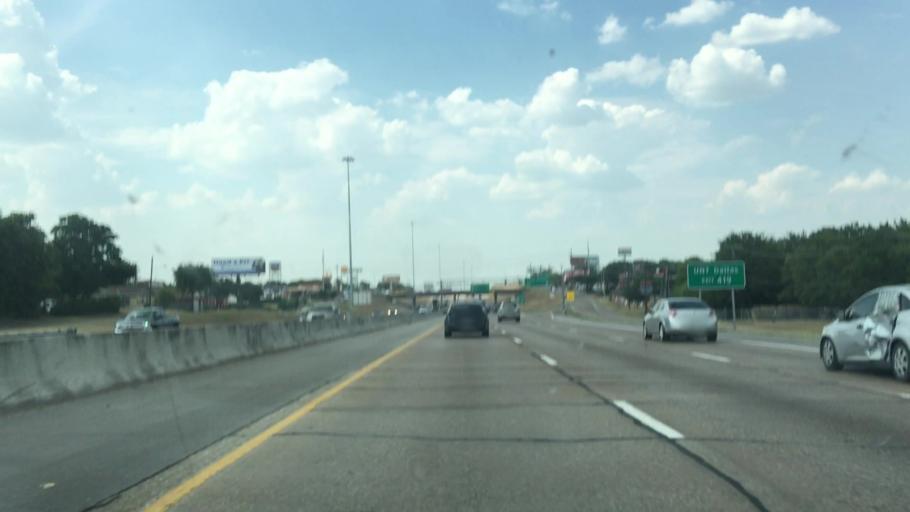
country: US
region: Texas
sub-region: Dallas County
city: DeSoto
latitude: 32.6588
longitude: -96.8230
